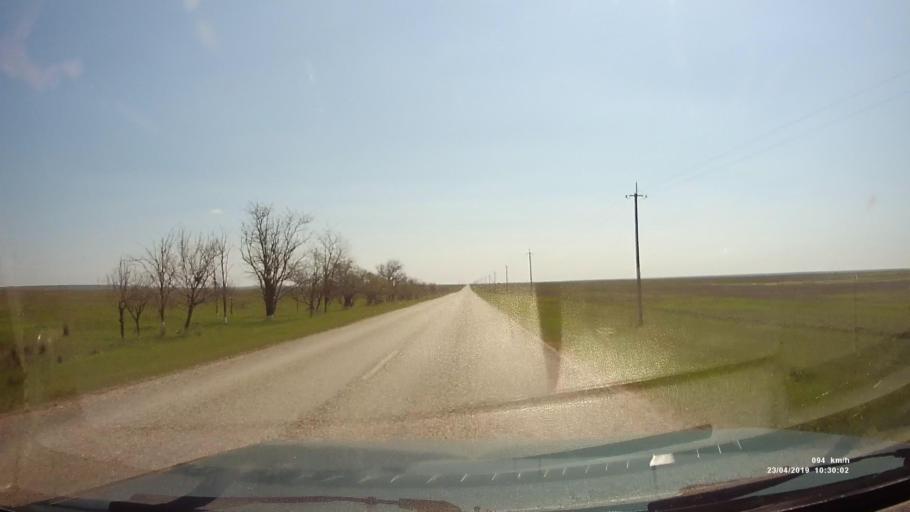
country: RU
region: Kalmykiya
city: Yashalta
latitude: 46.5949
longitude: 42.5373
